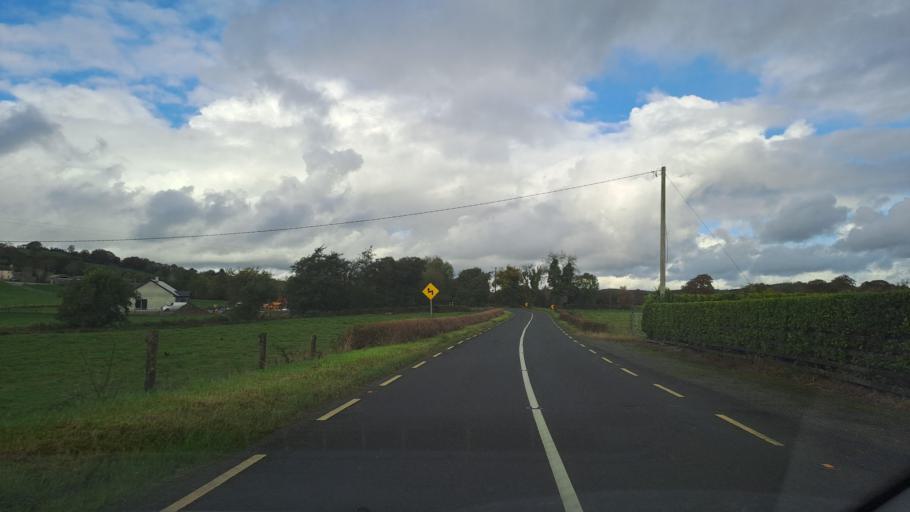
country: IE
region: Ulster
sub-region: An Cabhan
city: Mullagh
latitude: 53.8237
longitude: -6.9507
